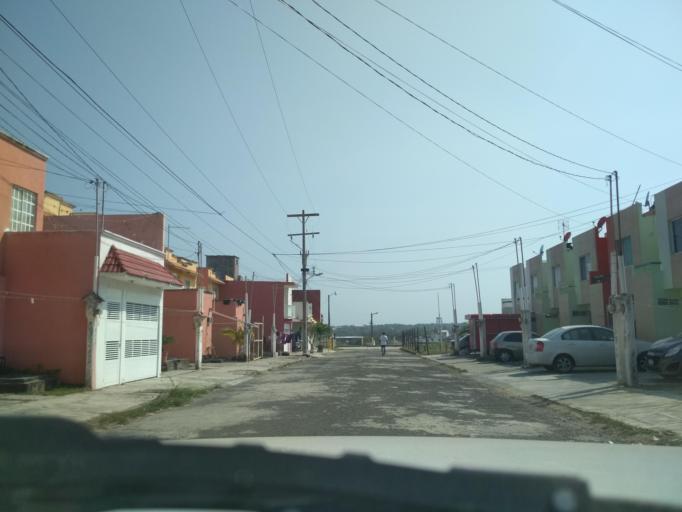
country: MX
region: Veracruz
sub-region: Veracruz
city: Colonia el Renacimiento
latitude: 19.2196
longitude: -96.2112
